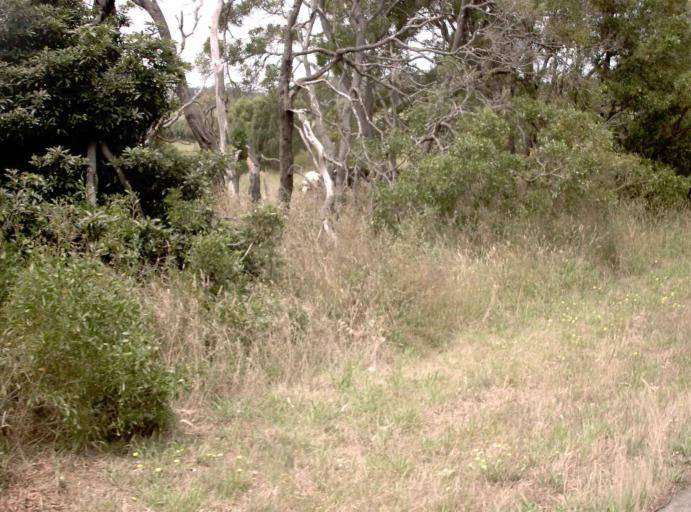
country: AU
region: Victoria
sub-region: Latrobe
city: Traralgon
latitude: -38.5011
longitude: 146.7111
